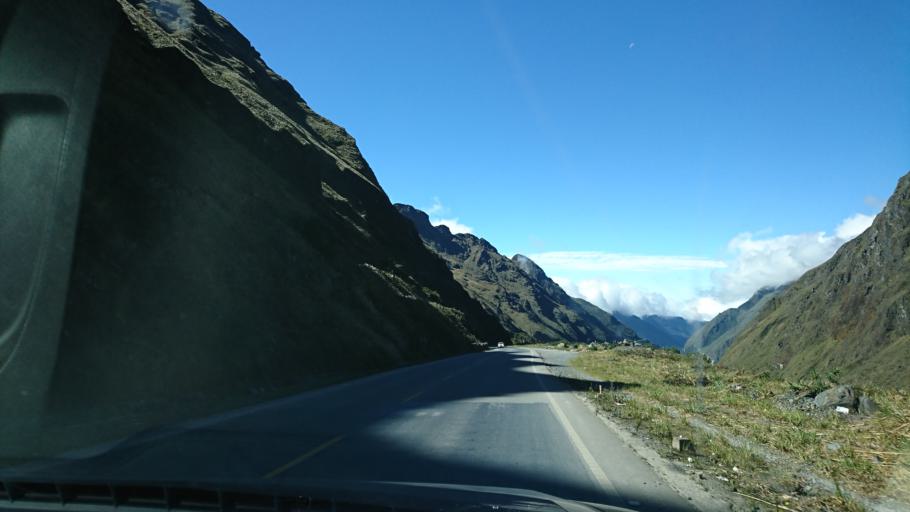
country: BO
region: La Paz
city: Coroico
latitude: -16.3219
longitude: -67.9346
